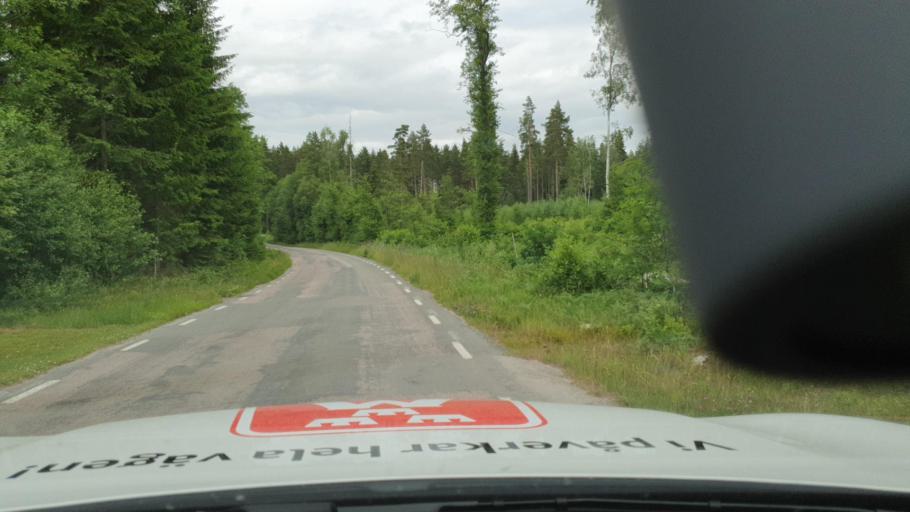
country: SE
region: Vaestra Goetaland
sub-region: Tidaholms Kommun
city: Tidaholm
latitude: 58.1838
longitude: 14.0046
